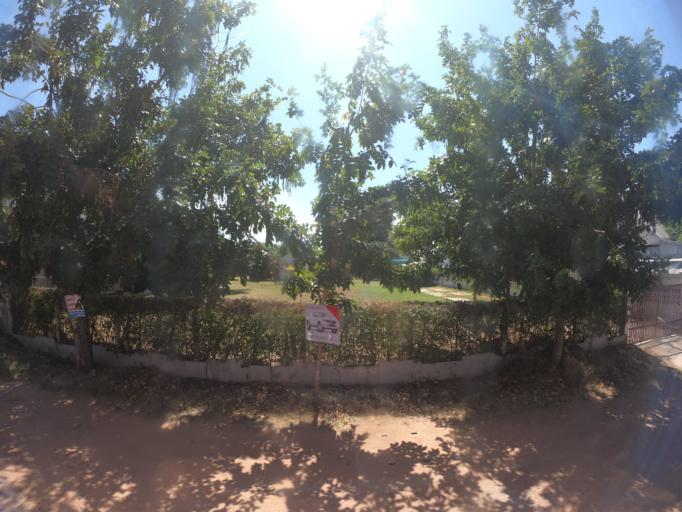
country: TH
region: Khon Kaen
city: Ban Phai
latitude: 16.0624
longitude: 102.7256
